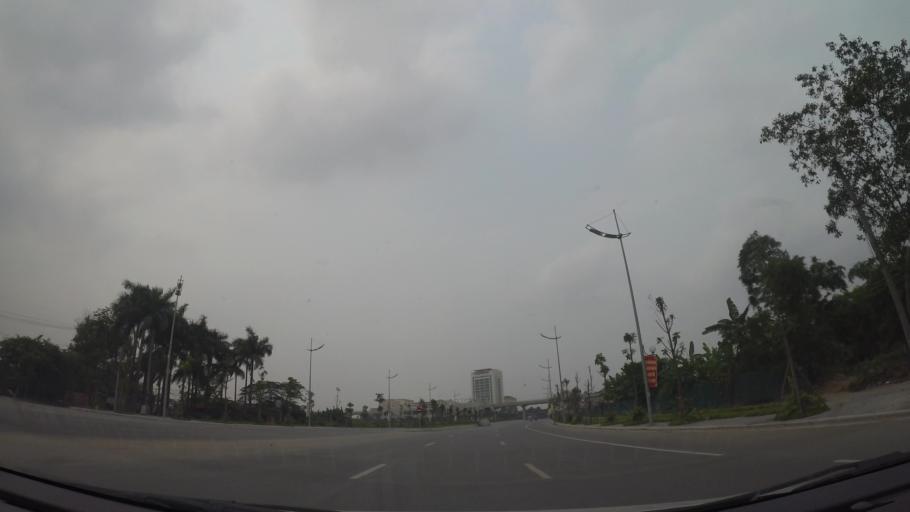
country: VN
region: Ha Noi
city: Cau Dien
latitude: 21.0493
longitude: 105.7354
